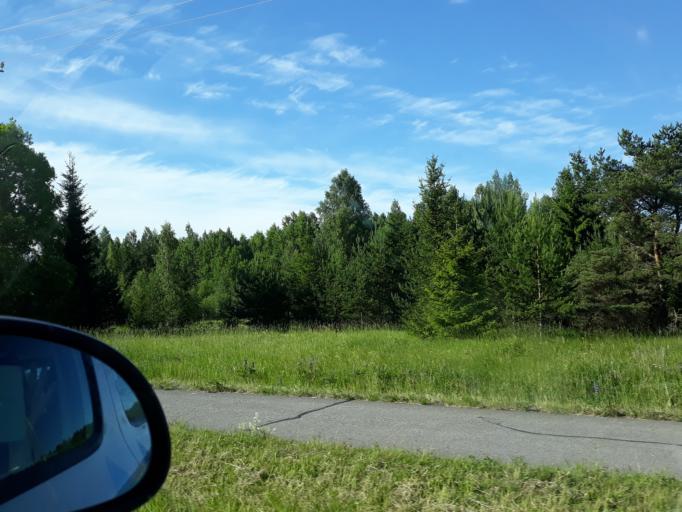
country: FI
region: Uusimaa
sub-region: Helsinki
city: Jaervenpaeae
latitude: 60.5472
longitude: 24.9816
